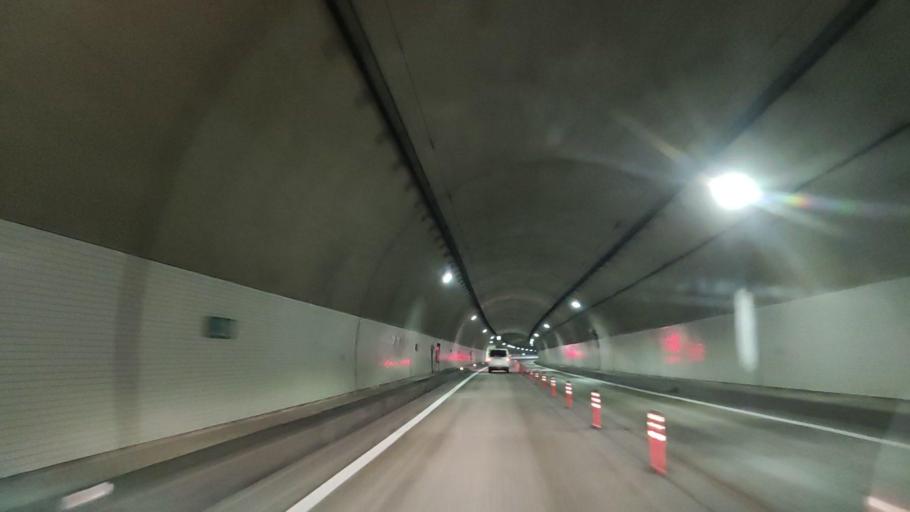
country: JP
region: Akita
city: Odate
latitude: 40.3351
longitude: 140.6121
